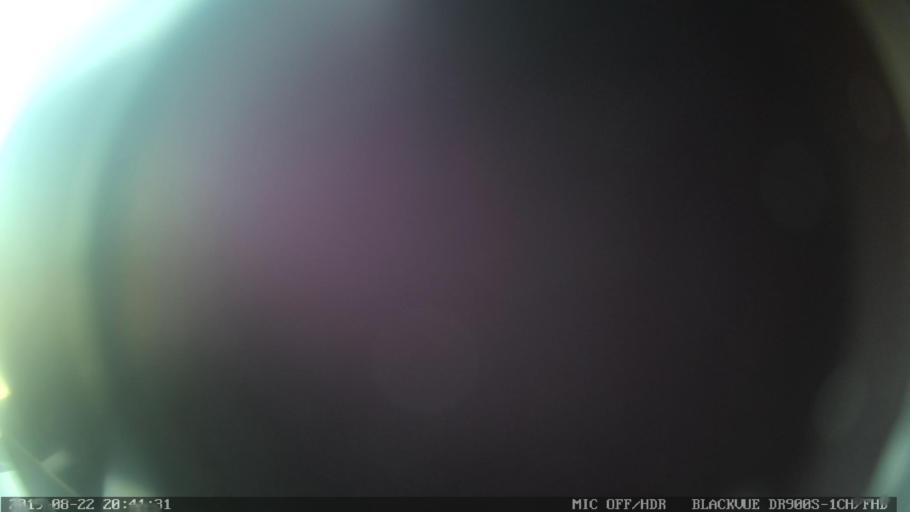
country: PT
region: Castelo Branco
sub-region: Proenca-A-Nova
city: Proenca-a-Nova
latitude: 39.6862
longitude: -7.8059
